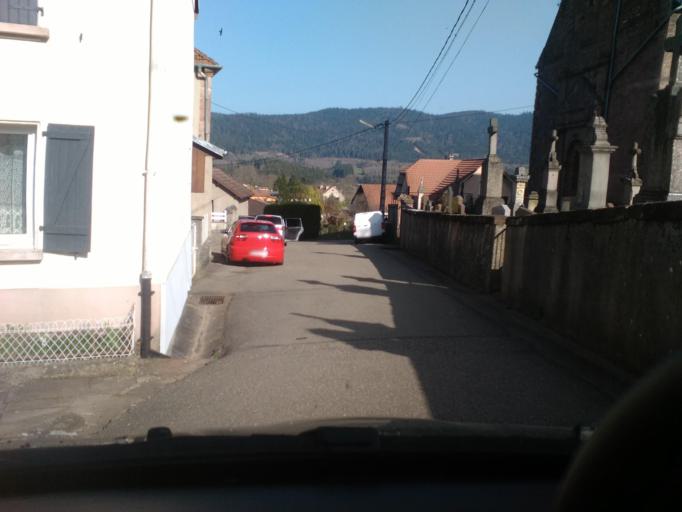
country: FR
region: Lorraine
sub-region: Departement des Vosges
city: Senones
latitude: 48.3919
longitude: 6.9946
